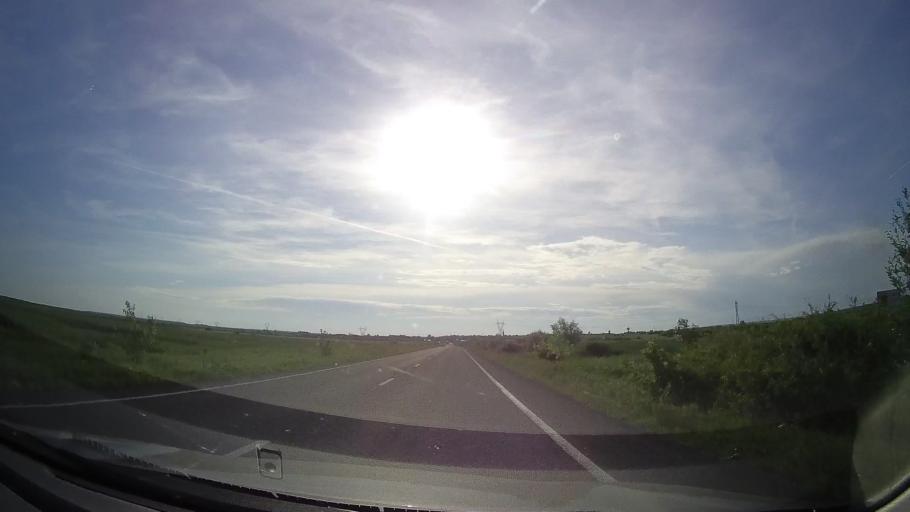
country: RO
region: Timis
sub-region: Oras Recas
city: Recas
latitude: 45.7956
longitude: 21.5333
